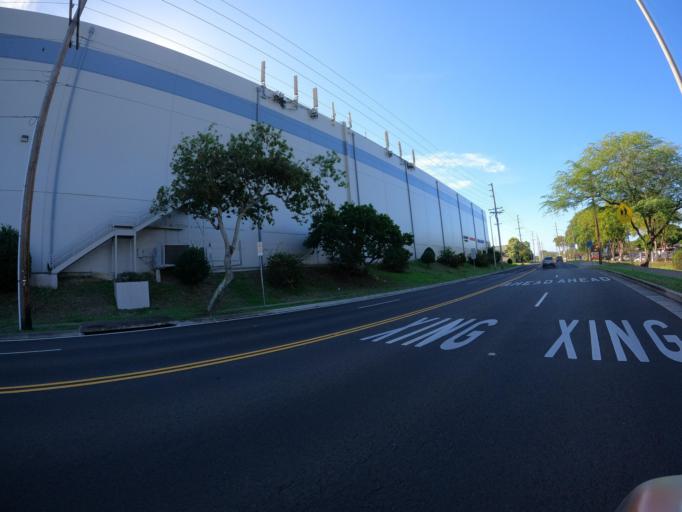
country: US
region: Hawaii
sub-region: Honolulu County
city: Halawa
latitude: 21.3574
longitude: -157.9293
